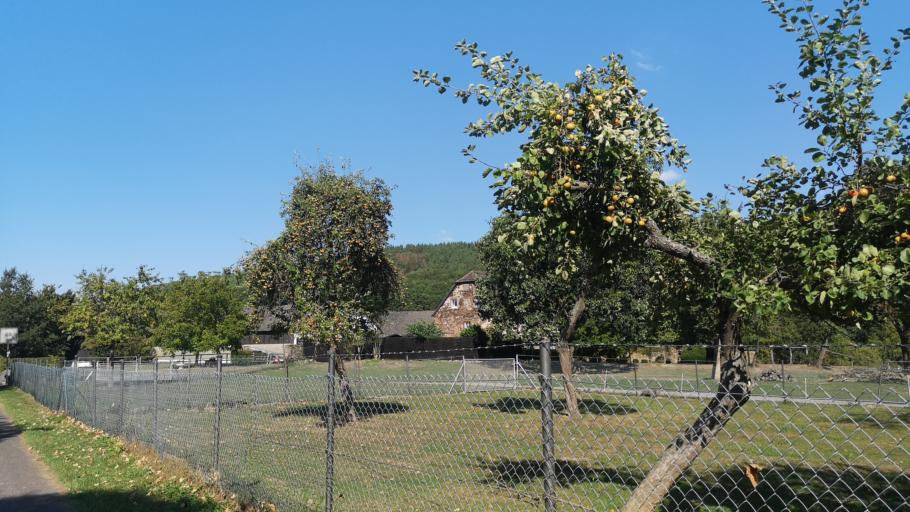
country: DE
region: North Rhine-Westphalia
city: Heimbach
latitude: 50.6580
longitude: 6.4840
